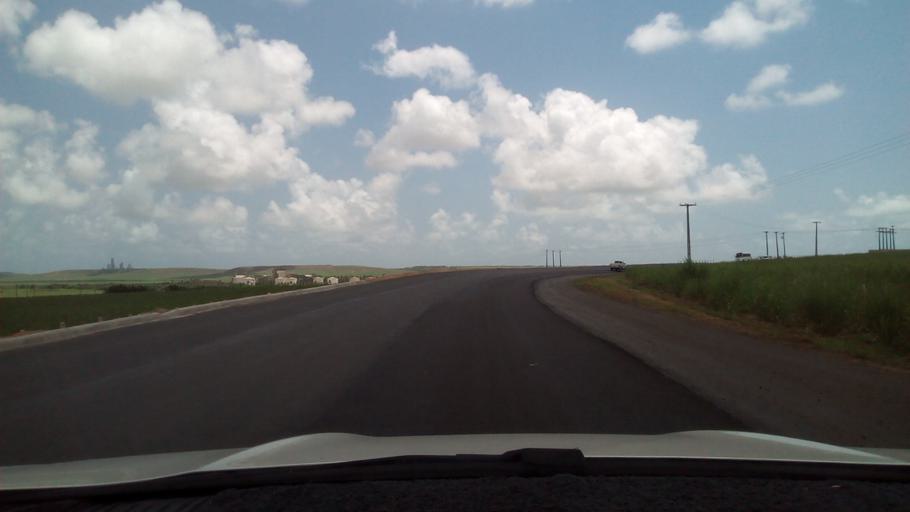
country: BR
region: Paraiba
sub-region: Caapora
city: Caapora
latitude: -7.5136
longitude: -34.8904
